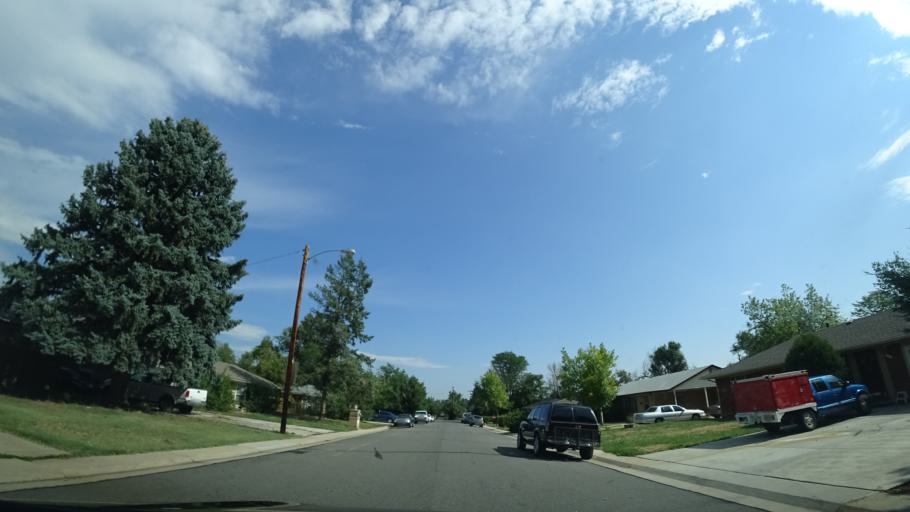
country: US
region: Colorado
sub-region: Jefferson County
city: Lakewood
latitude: 39.7172
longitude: -105.0569
